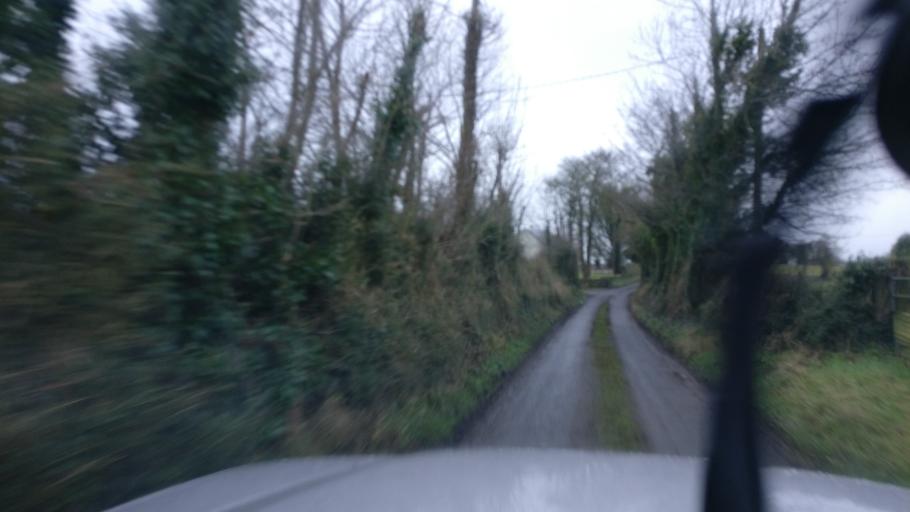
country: IE
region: Connaught
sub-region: County Galway
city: Loughrea
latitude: 53.1884
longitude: -8.6144
